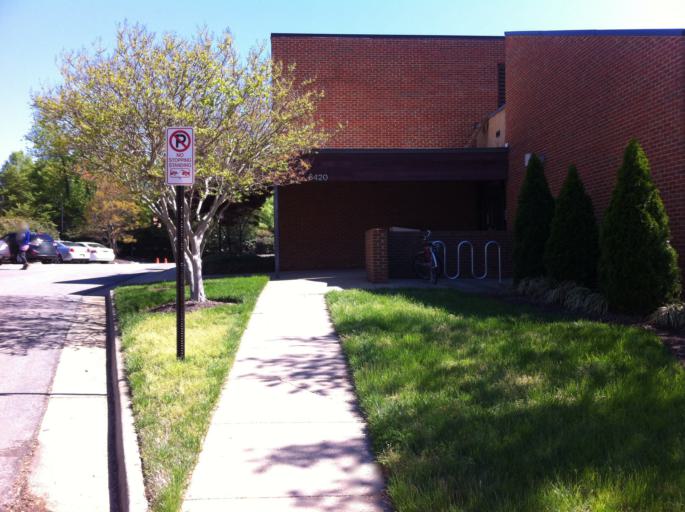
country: US
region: Virginia
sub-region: Henrico County
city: Dumbarton
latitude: 37.5776
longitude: -77.5115
